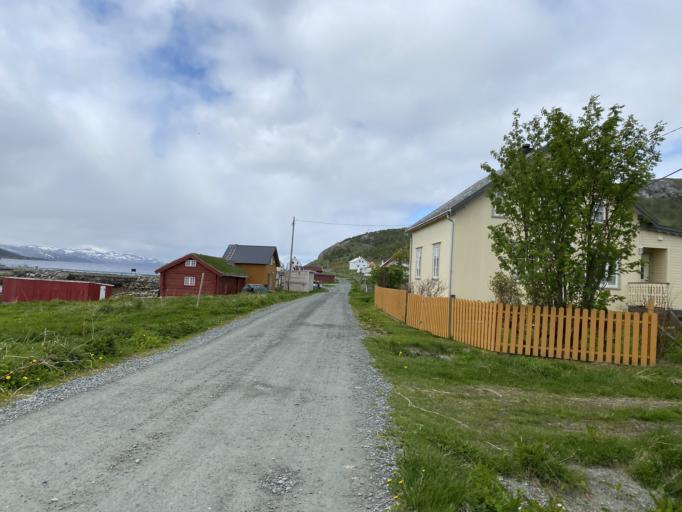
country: NO
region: Troms
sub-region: Karlsoy
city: Hansnes
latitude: 70.0017
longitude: 19.8930
